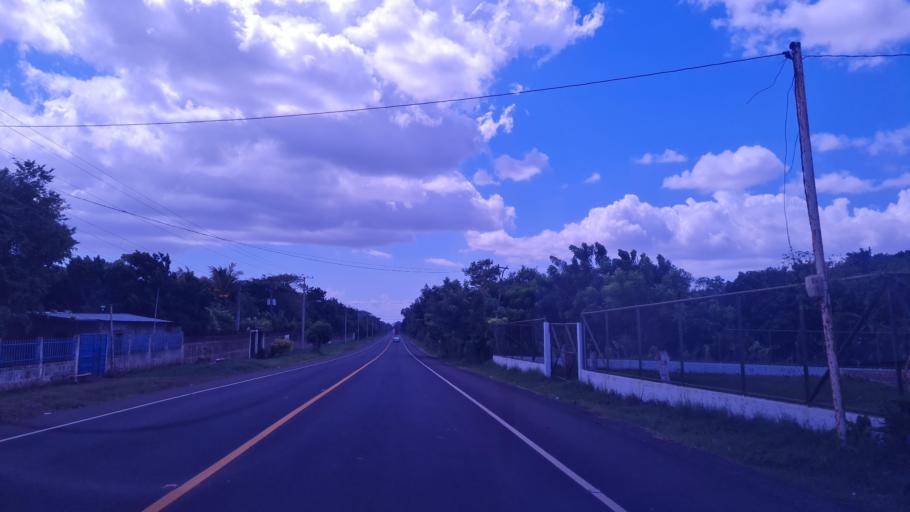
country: NI
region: Masaya
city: Nindiri
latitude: 12.0257
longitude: -86.1212
